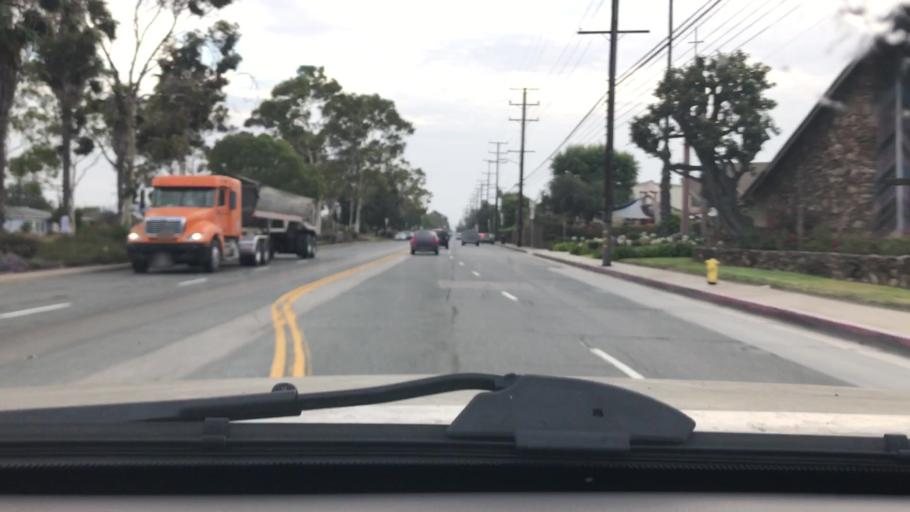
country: US
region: California
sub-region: Los Angeles County
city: Marina del Rey
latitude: 33.9863
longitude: -118.4247
